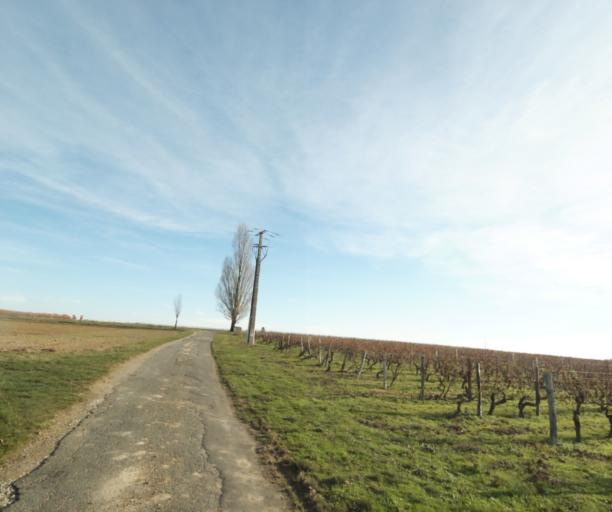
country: FR
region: Poitou-Charentes
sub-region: Departement de la Charente-Maritime
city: Chaniers
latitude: 45.7245
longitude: -0.5286
